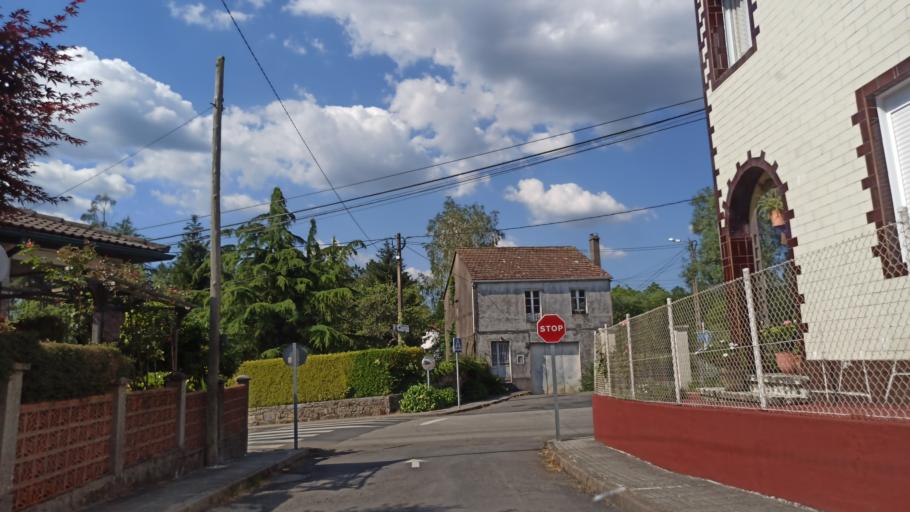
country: ES
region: Galicia
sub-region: Provincia da Coruna
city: Negreira
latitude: 42.9138
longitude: -8.7405
